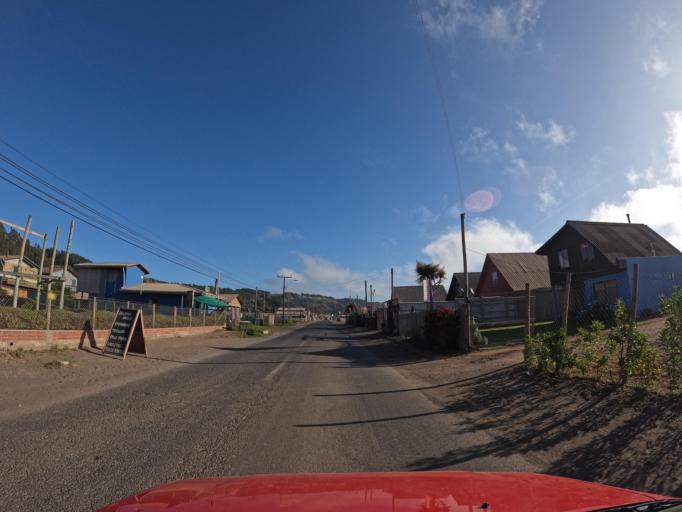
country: CL
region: Maule
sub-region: Provincia de Talca
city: Constitucion
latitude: -34.9299
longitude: -72.1799
